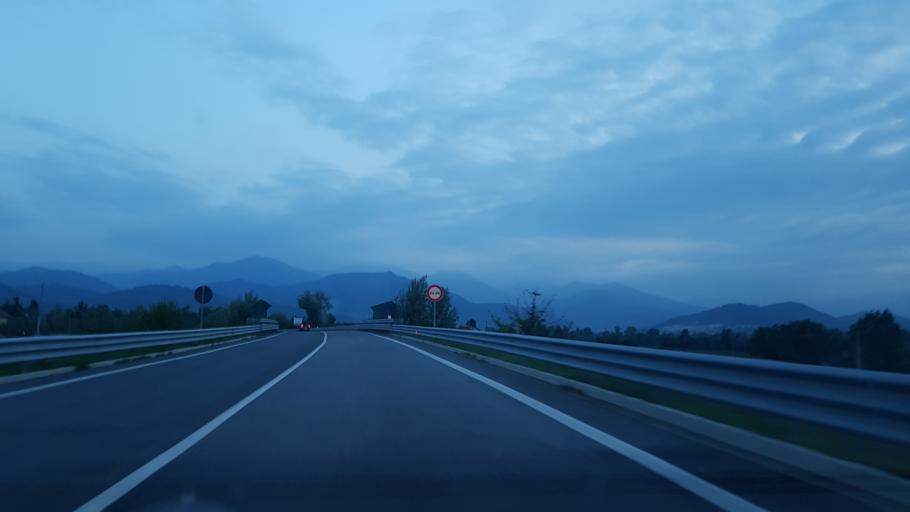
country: IT
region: Piedmont
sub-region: Provincia di Cuneo
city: Mondovi
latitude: 44.3775
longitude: 7.7903
